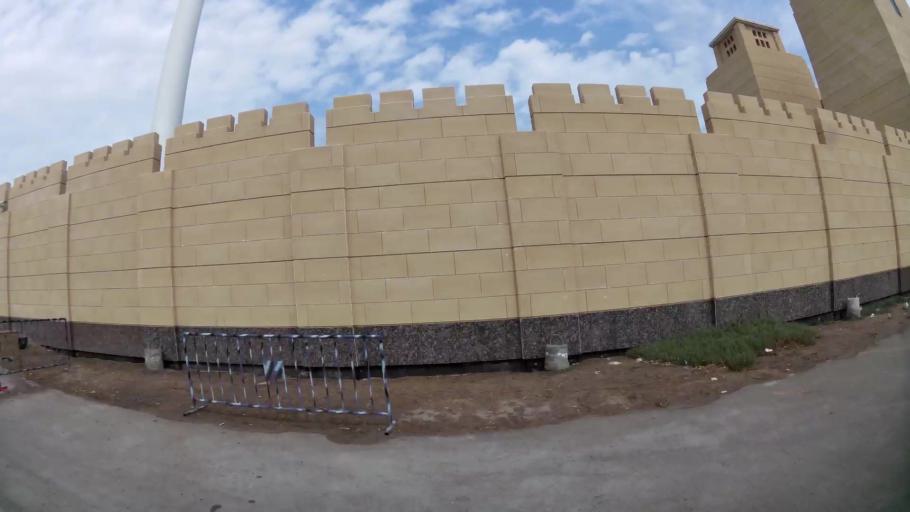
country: AE
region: Abu Dhabi
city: Abu Dhabi
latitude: 24.4101
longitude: 54.4649
